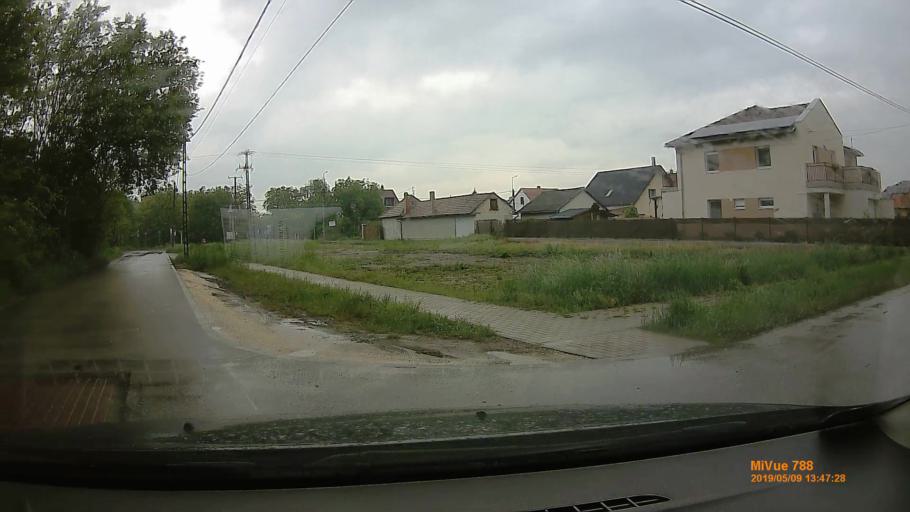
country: HU
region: Budapest
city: Budapest XVI. keruelet
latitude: 47.5289
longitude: 19.1863
